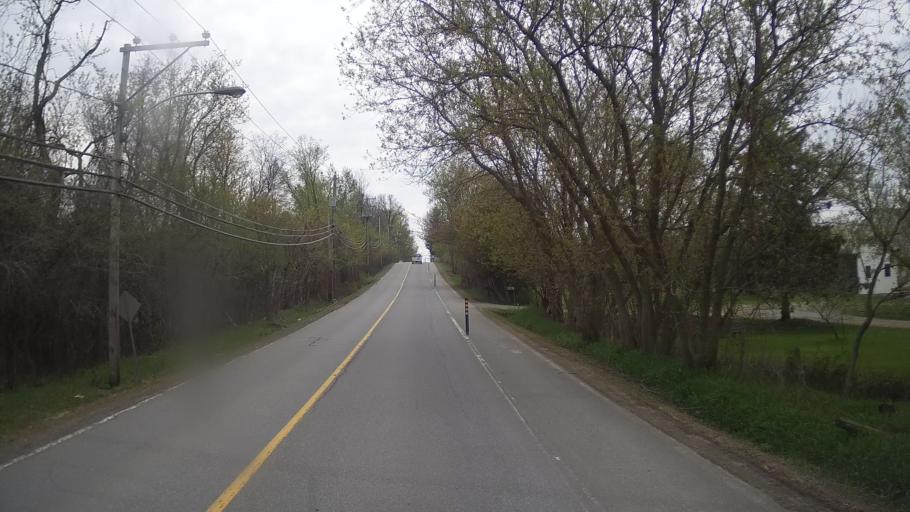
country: CA
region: Quebec
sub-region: Monteregie
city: Hudson
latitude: 45.4443
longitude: -74.1688
